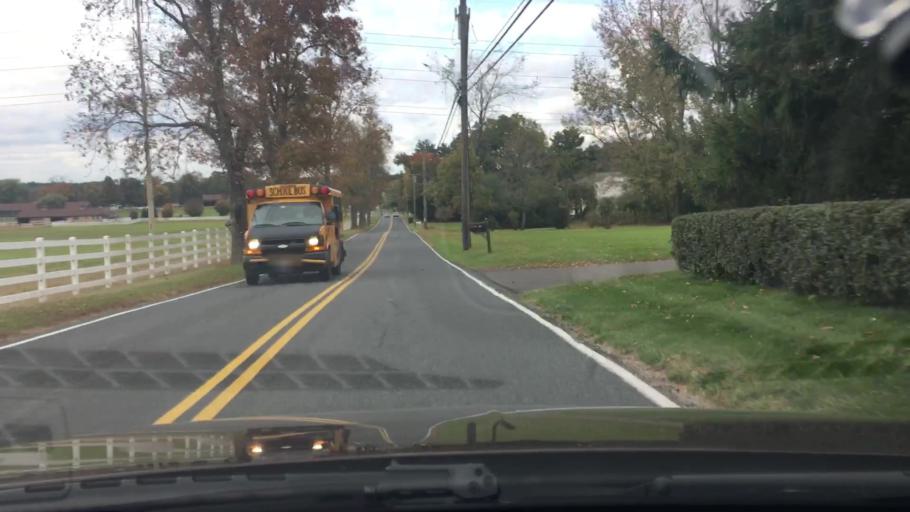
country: US
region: Connecticut
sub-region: Tolland County
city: Somers
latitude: 41.9744
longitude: -72.4841
